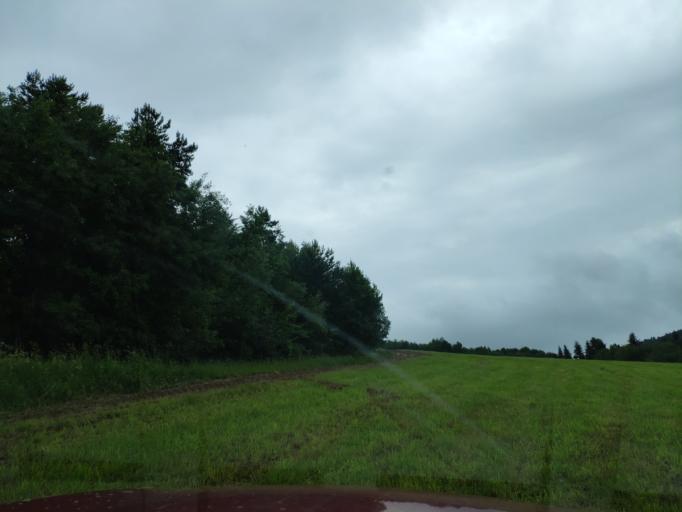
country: SK
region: Presovsky
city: Sabinov
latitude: 49.0544
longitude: 21.0109
